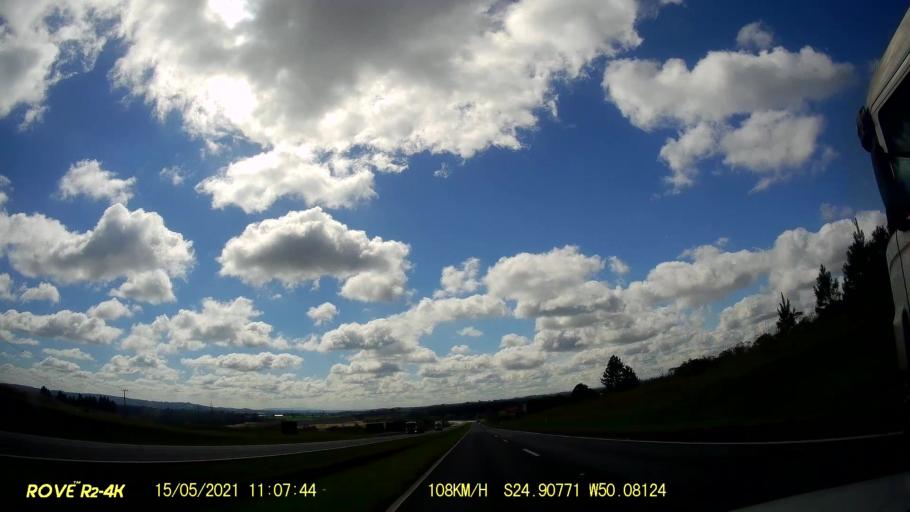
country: BR
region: Parana
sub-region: Carambei
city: Carambei
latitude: -24.9079
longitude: -50.0815
